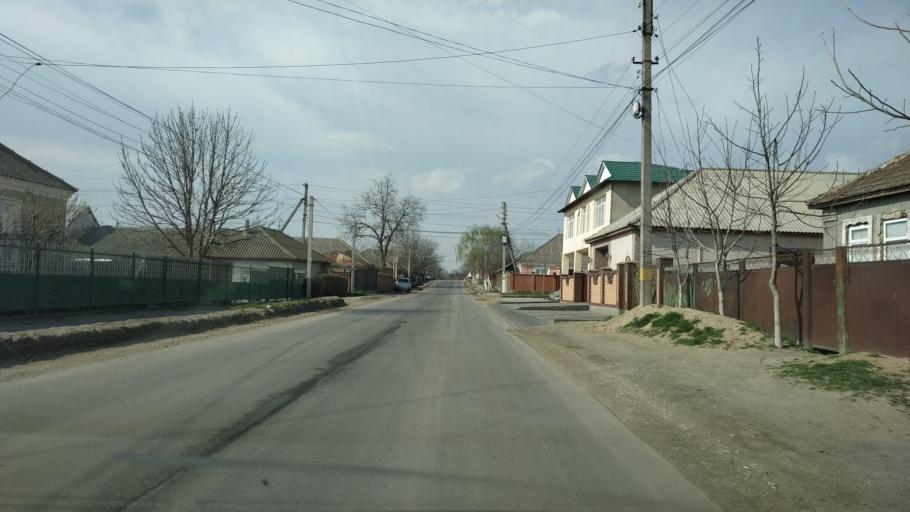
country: MD
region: Gagauzia
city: Vulcanesti
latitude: 45.6763
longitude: 28.4154
